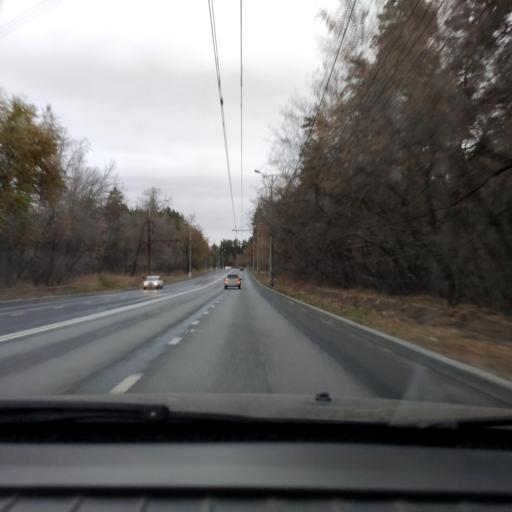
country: RU
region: Samara
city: Zhigulevsk
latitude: 53.4915
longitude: 49.4628
